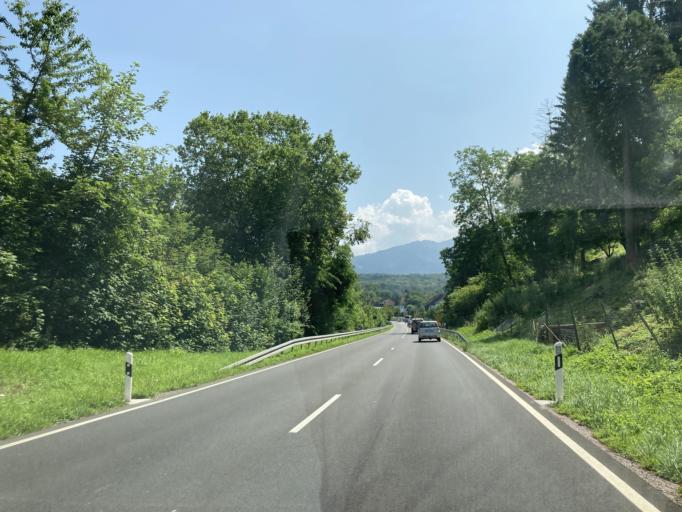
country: DE
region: Baden-Wuerttemberg
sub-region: Freiburg Region
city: Mullheim
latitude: 47.8052
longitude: 7.6221
